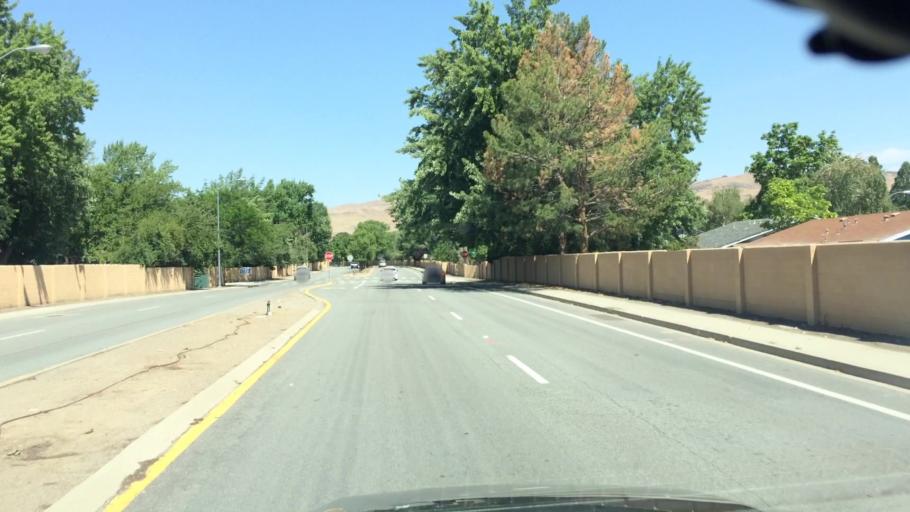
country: US
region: Nevada
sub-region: Washoe County
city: Sparks
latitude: 39.5564
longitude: -119.7168
